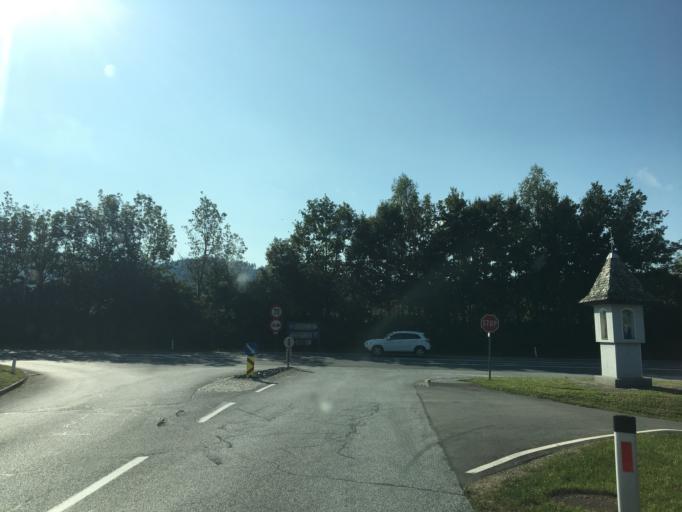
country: AT
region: Carinthia
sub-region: Politischer Bezirk Volkermarkt
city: Griffen
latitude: 46.6896
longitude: 14.7024
